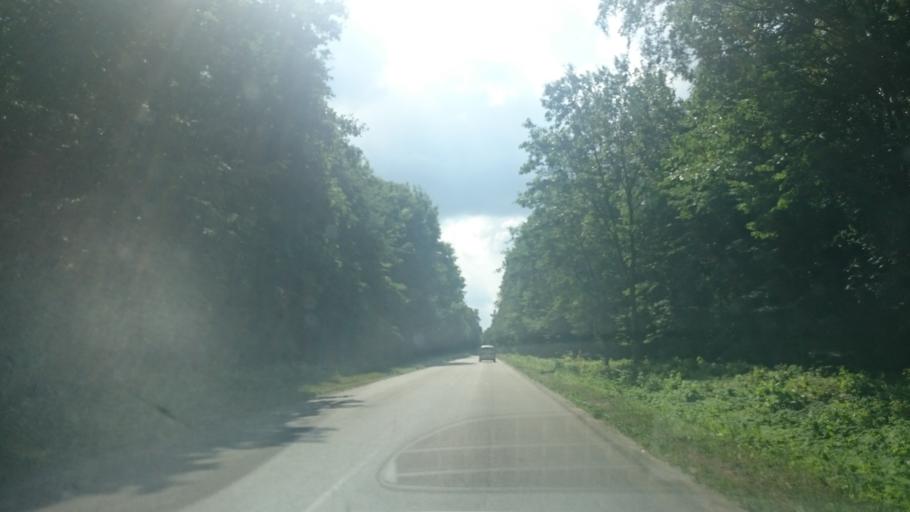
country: PL
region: Pomeranian Voivodeship
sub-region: Powiat starogardzki
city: Zblewo
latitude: 53.9660
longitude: 18.2847
